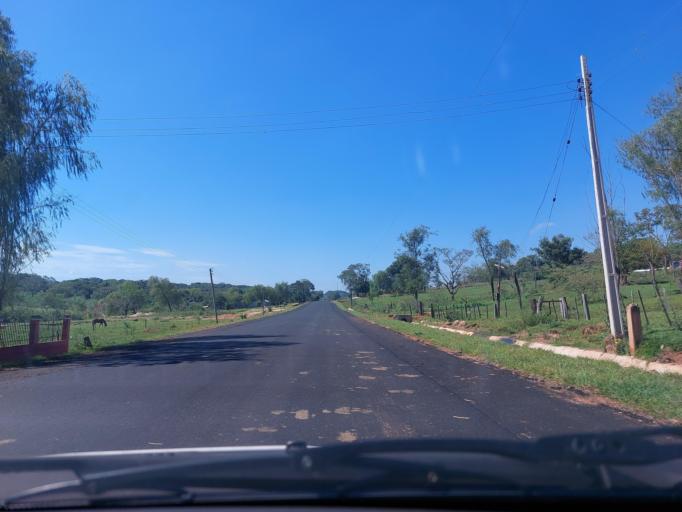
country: PY
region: San Pedro
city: Guayaybi
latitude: -24.5501
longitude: -56.5180
